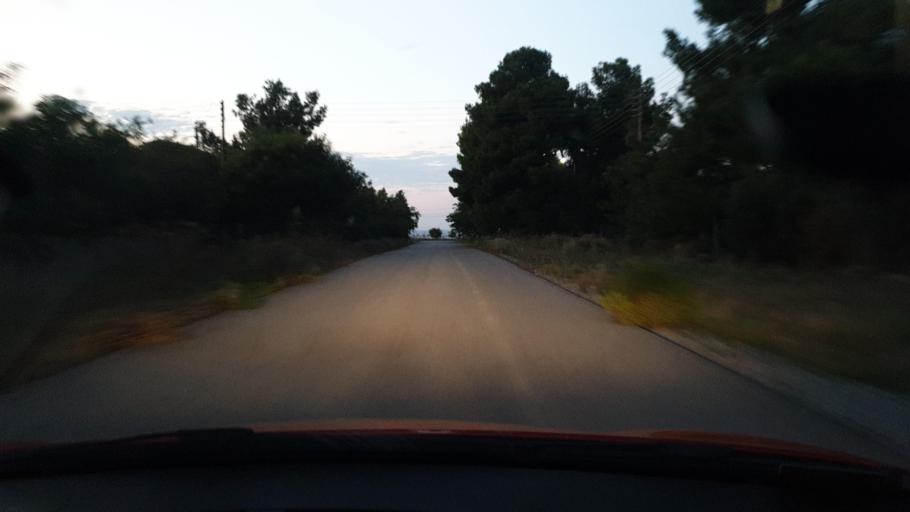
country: GR
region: Central Macedonia
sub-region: Nomos Thessalonikis
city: Agia Triada
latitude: 40.5047
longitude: 22.8325
